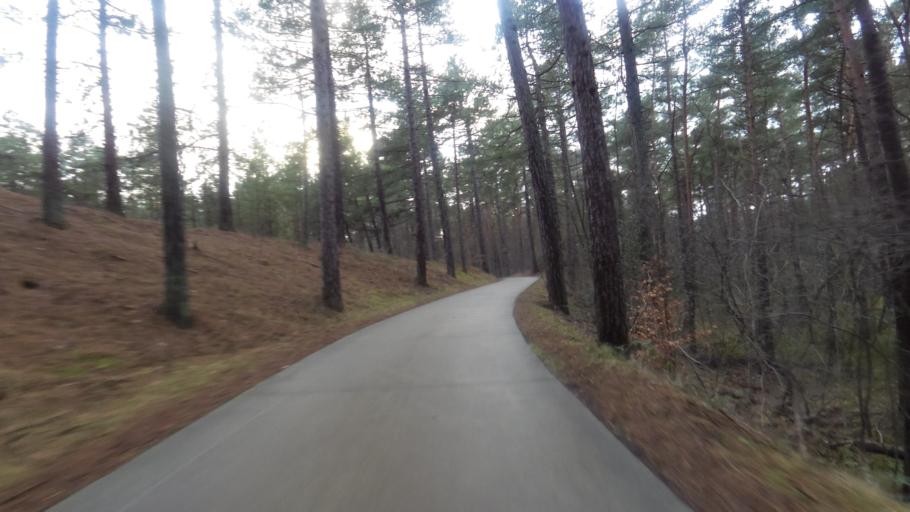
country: NL
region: North Holland
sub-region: Gemeente Bergen
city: Egmond aan Zee
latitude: 52.6845
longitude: 4.6788
